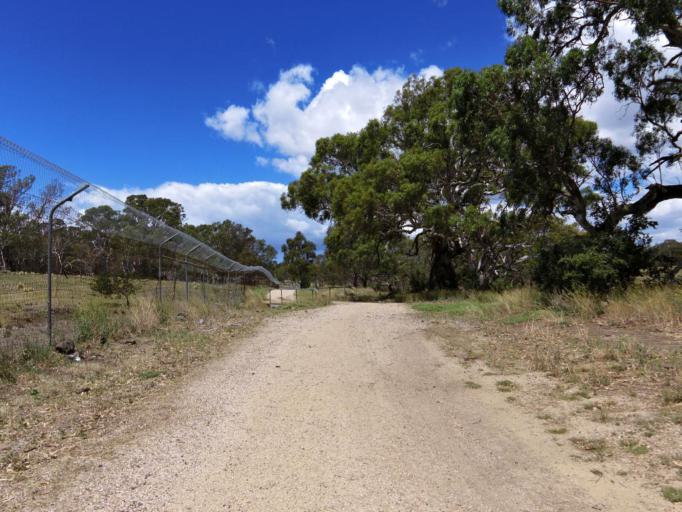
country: AU
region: Victoria
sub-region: Hume
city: Greenvale
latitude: -37.6590
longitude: 144.8582
